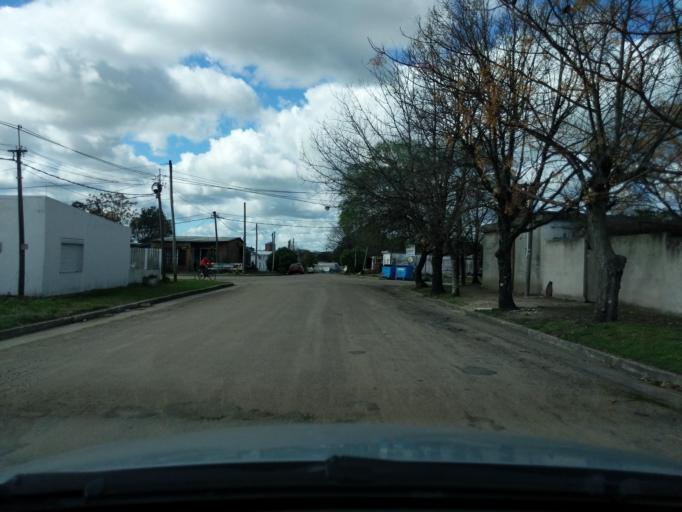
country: UY
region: Florida
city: Florida
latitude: -34.0944
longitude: -56.2304
